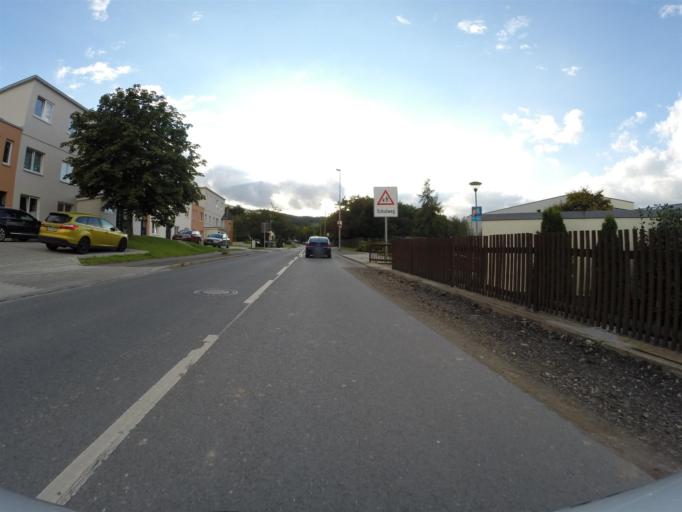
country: DE
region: Thuringia
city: Jena
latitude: 50.8927
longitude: 11.5819
